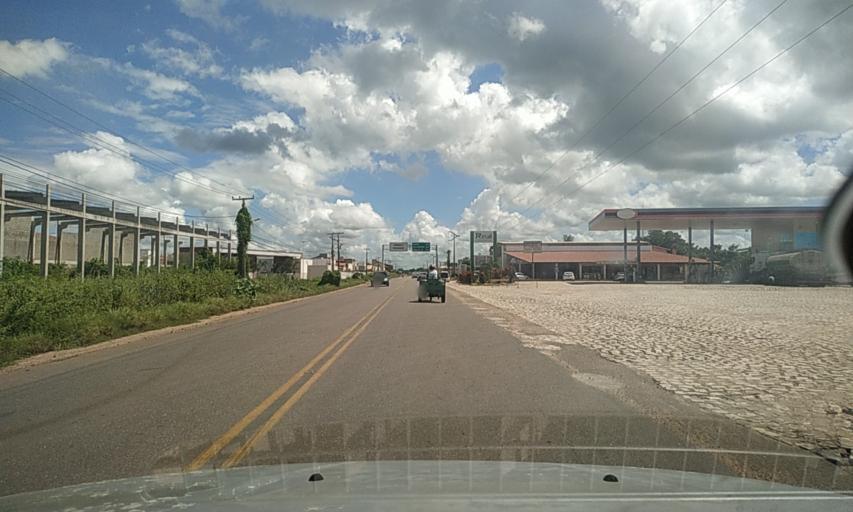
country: BR
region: Rio Grande do Norte
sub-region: Mossoro
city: Mossoro
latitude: -5.1895
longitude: -37.3772
